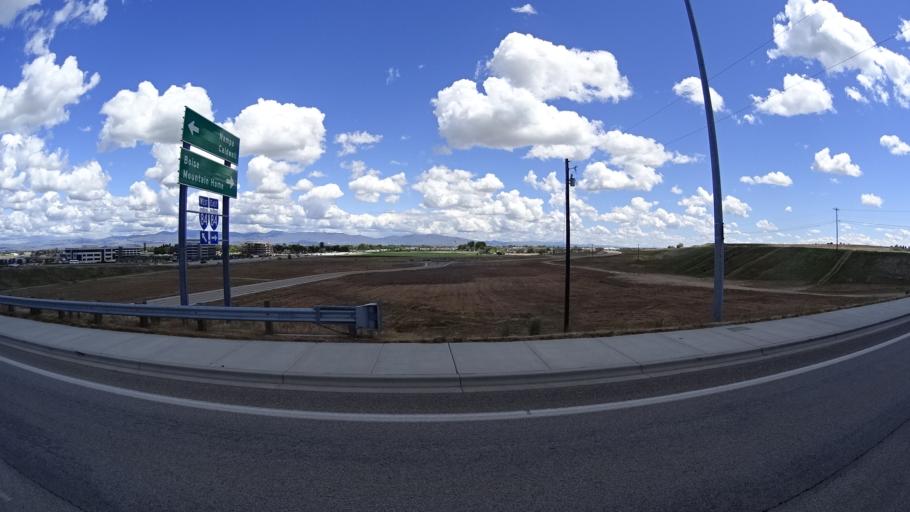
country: US
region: Idaho
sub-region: Ada County
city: Meridian
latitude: 43.5911
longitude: -116.4339
